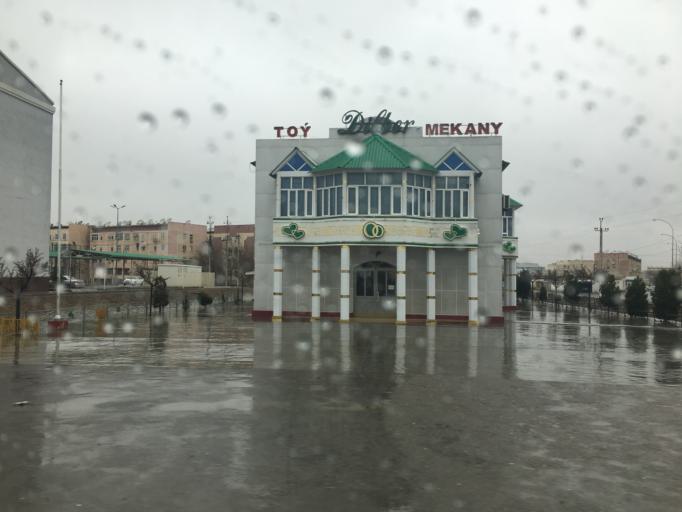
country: TM
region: Mary
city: Mary
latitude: 37.5770
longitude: 61.8347
